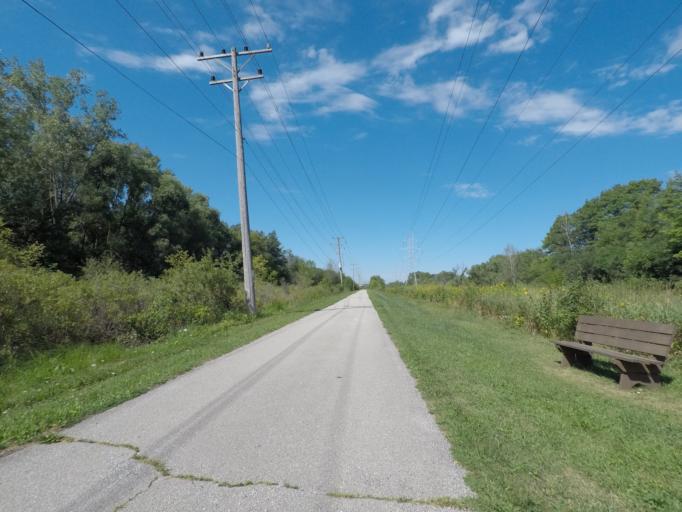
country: US
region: Wisconsin
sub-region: Waukesha County
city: Waukesha
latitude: 43.0099
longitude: -88.1920
